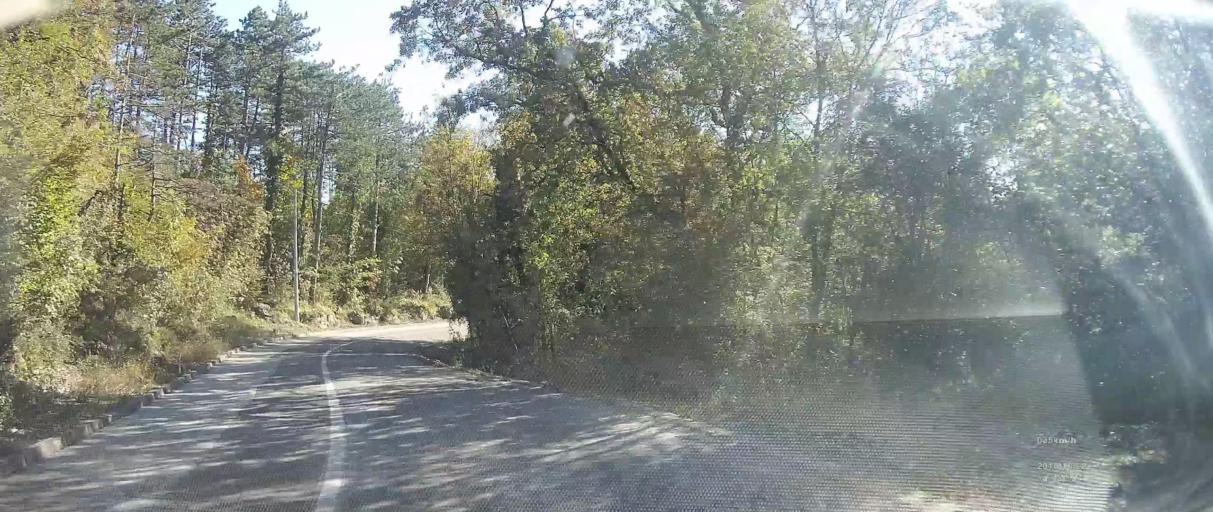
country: HR
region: Primorsko-Goranska
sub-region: Grad Opatija
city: Opatija
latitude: 45.3311
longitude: 14.2753
